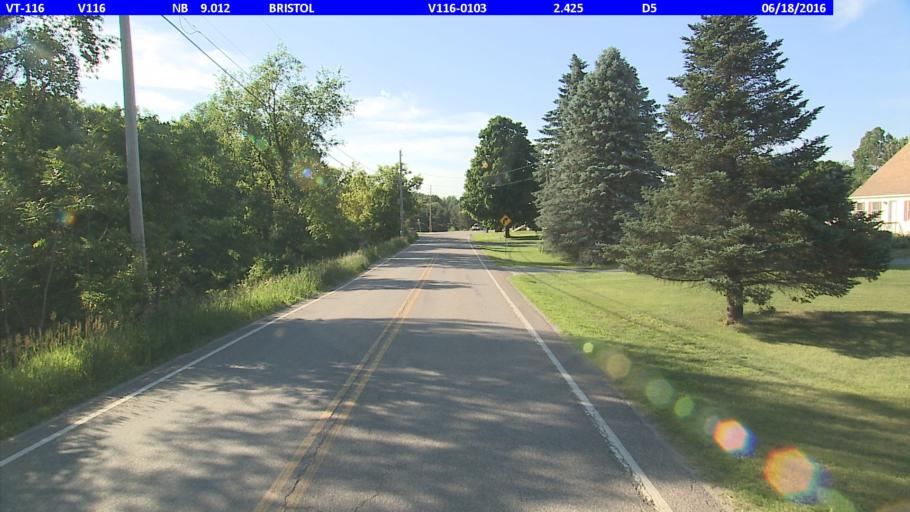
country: US
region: Vermont
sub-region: Addison County
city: Bristol
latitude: 44.0883
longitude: -73.0906
